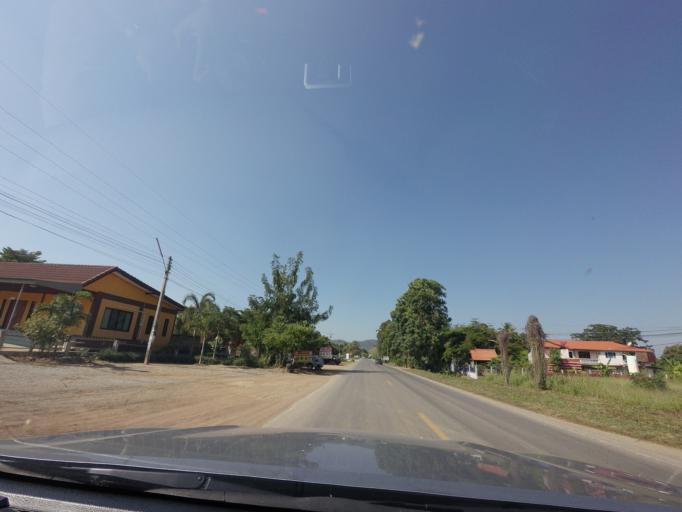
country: TH
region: Sukhothai
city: Sawankhalok
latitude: 17.3817
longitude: 99.7938
